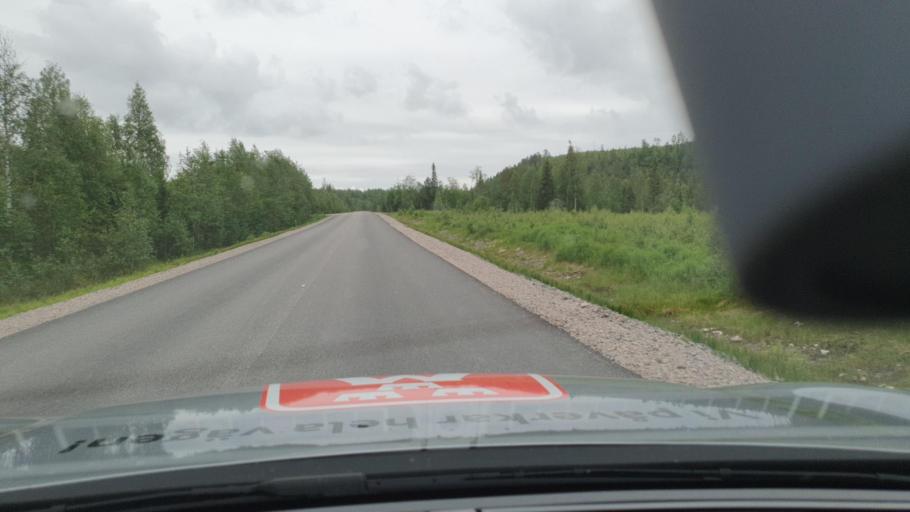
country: SE
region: Norrbotten
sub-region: Overtornea Kommun
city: OEvertornea
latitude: 66.5339
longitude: 23.3650
